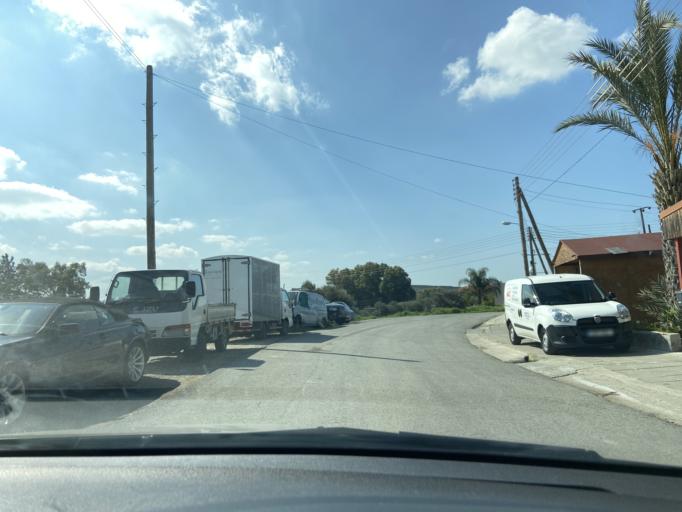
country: CY
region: Lefkosia
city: Alampra
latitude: 35.0196
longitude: 33.3851
